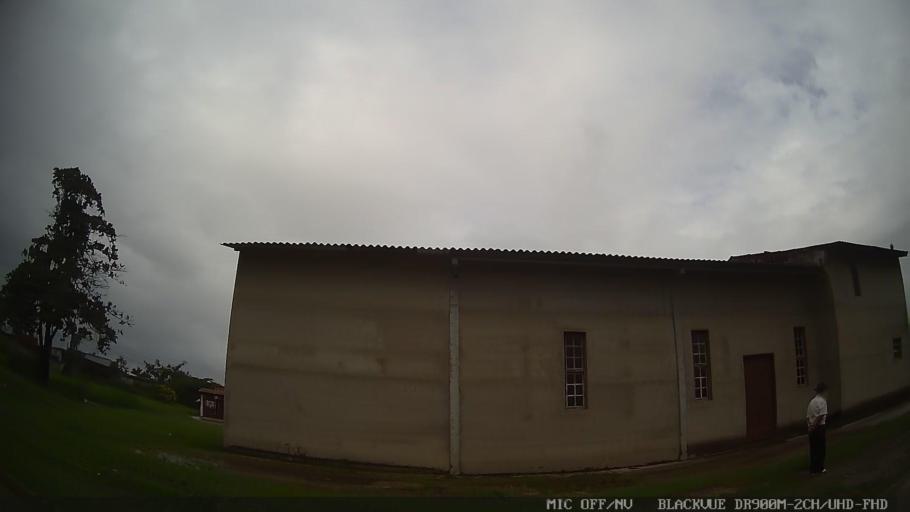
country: BR
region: Sao Paulo
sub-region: Itanhaem
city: Itanhaem
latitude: -24.1763
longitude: -46.8170
